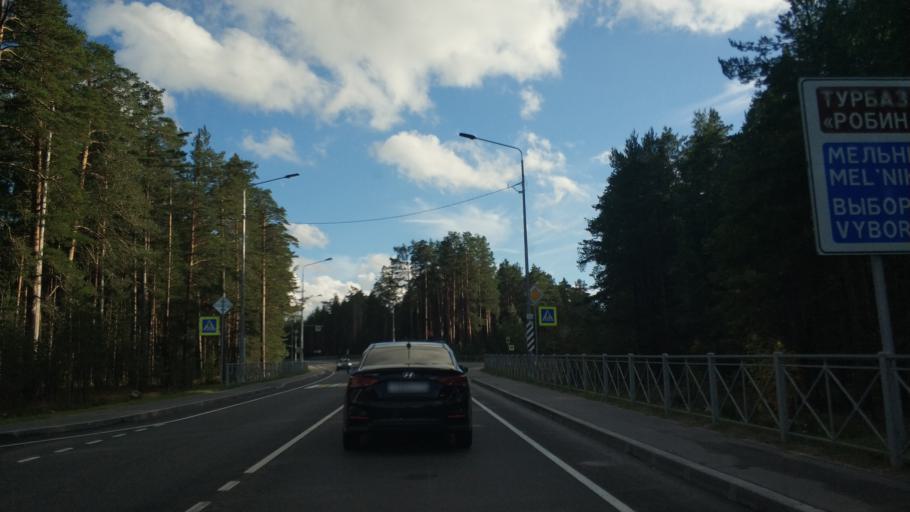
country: RU
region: Leningrad
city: Priozersk
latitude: 60.9978
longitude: 30.1823
